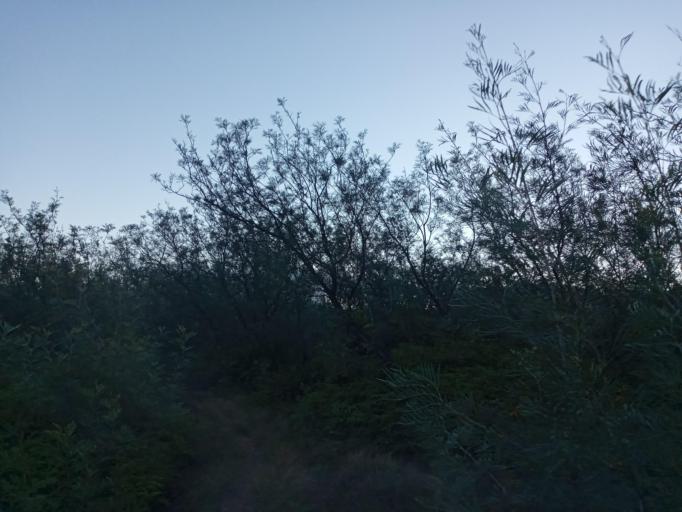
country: MG
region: Anosy
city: Fort Dauphin
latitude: -24.5115
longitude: 47.2228
